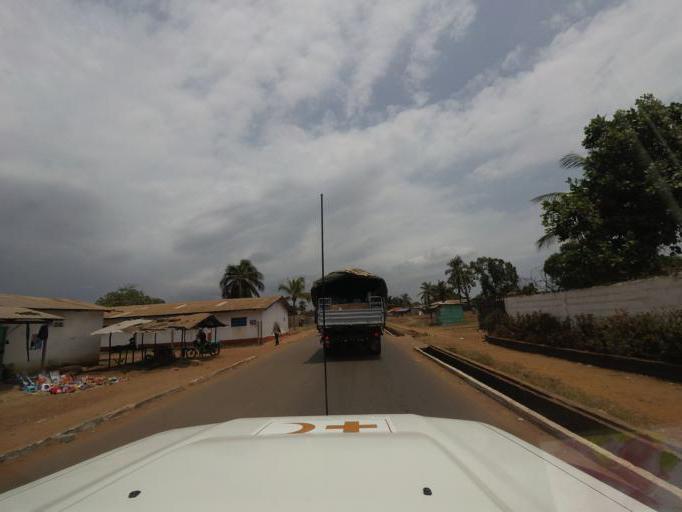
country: LR
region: Montserrado
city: Monrovia
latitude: 6.3059
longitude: -10.6917
